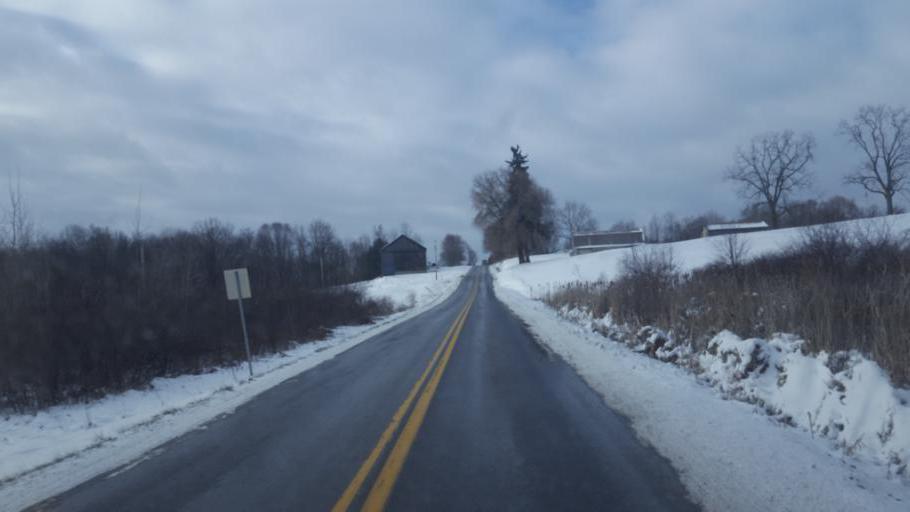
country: US
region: Pennsylvania
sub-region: Mercer County
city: Mercer
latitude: 41.1712
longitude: -80.2487
